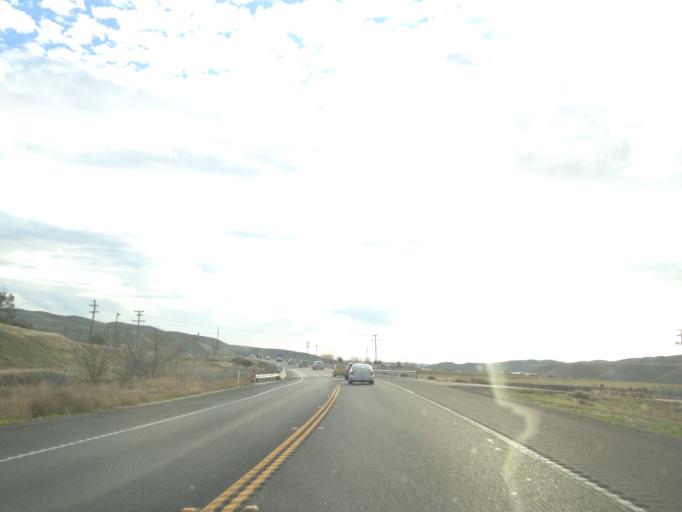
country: US
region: California
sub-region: San Luis Obispo County
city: Shandon
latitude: 35.6895
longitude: -120.3352
